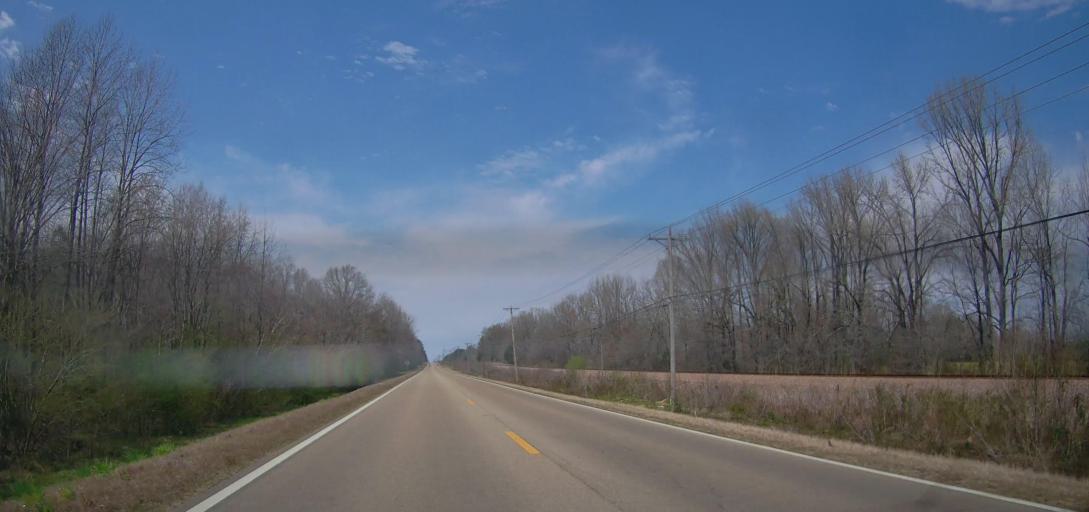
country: US
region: Mississippi
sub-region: Union County
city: New Albany
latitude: 34.5234
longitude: -89.0610
